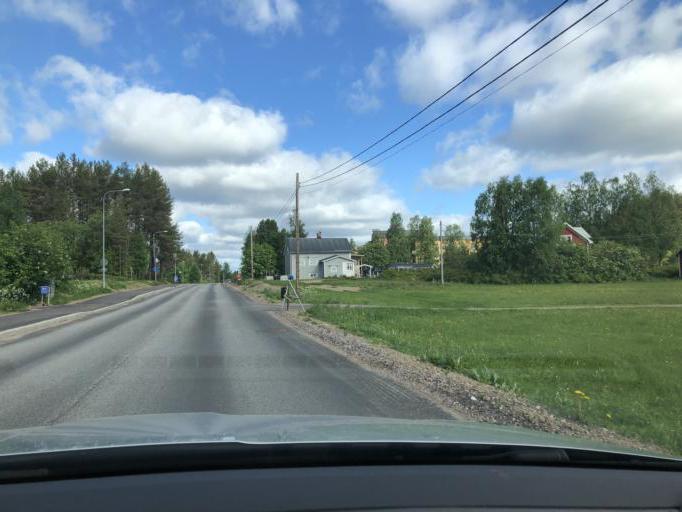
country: SE
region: Norrbotten
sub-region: Pajala Kommun
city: Pajala
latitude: 67.2219
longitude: 23.3456
